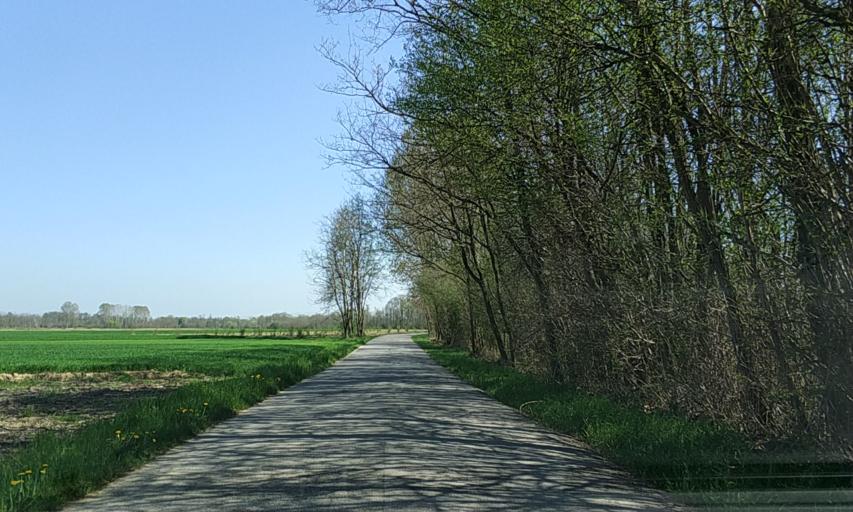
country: IT
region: Piedmont
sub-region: Provincia di Torino
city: Rivara
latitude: 45.3155
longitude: 7.6398
